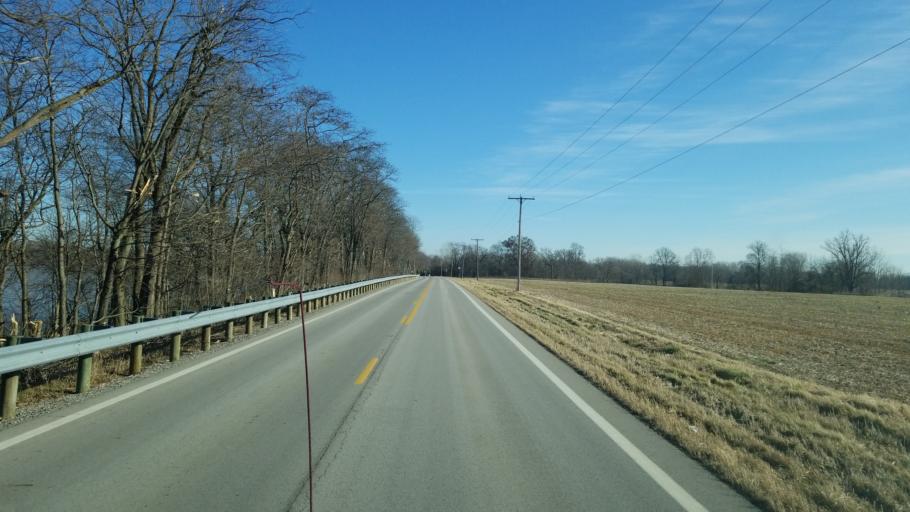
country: US
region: Ohio
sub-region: Henry County
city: Liberty Center
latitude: 41.4150
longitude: -83.9290
